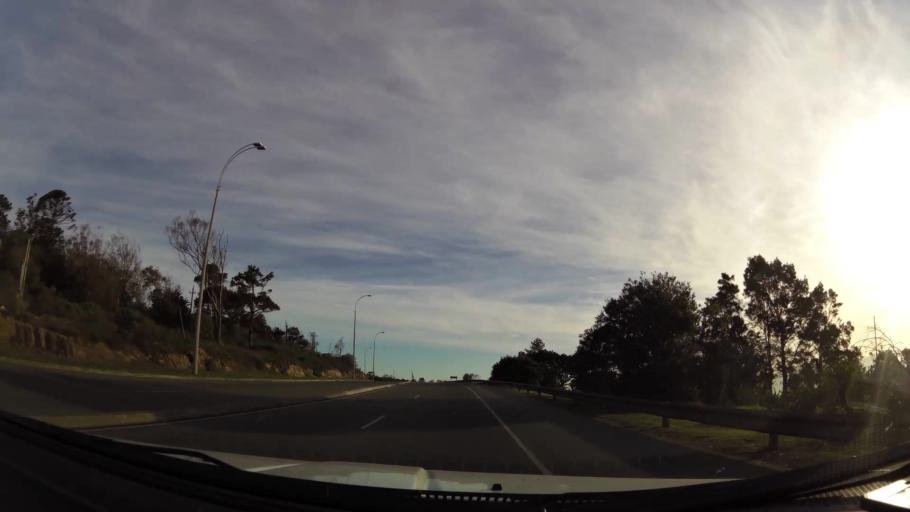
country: UY
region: Maldonado
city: Maldonado
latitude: -34.8935
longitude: -55.0381
